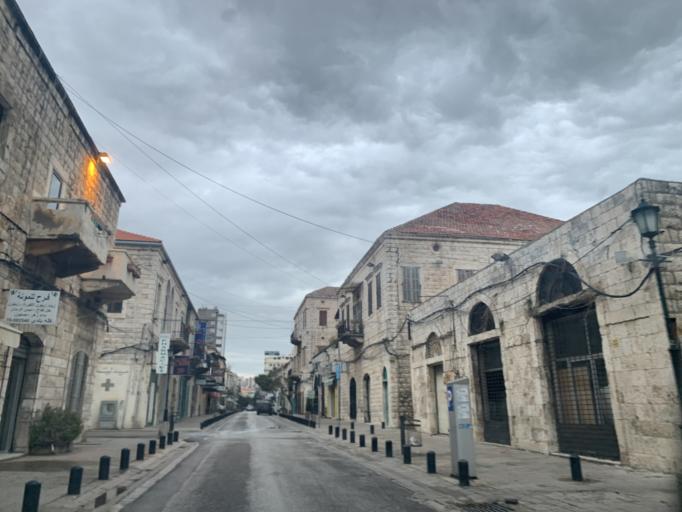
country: LB
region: Mont-Liban
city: Djounie
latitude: 33.9868
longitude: 35.6362
